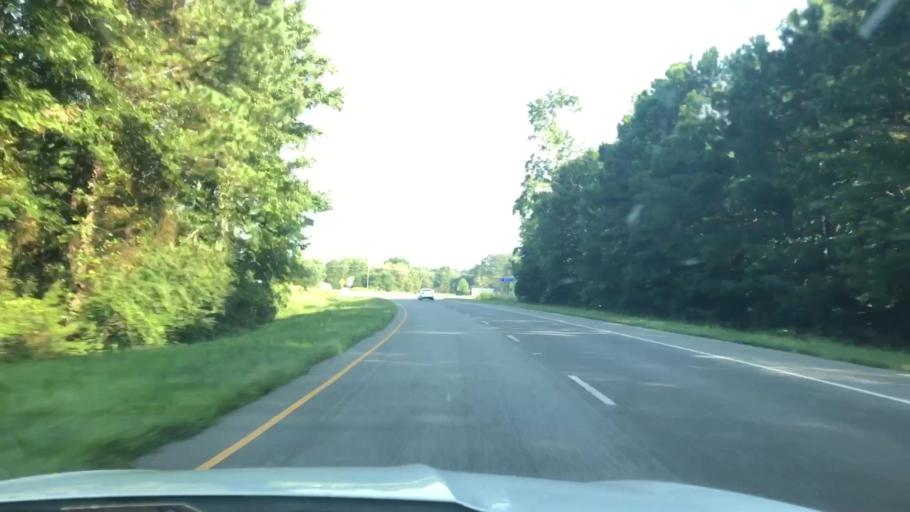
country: US
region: Virginia
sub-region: Essex County
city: Tappahannock
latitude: 37.8009
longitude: -76.7741
